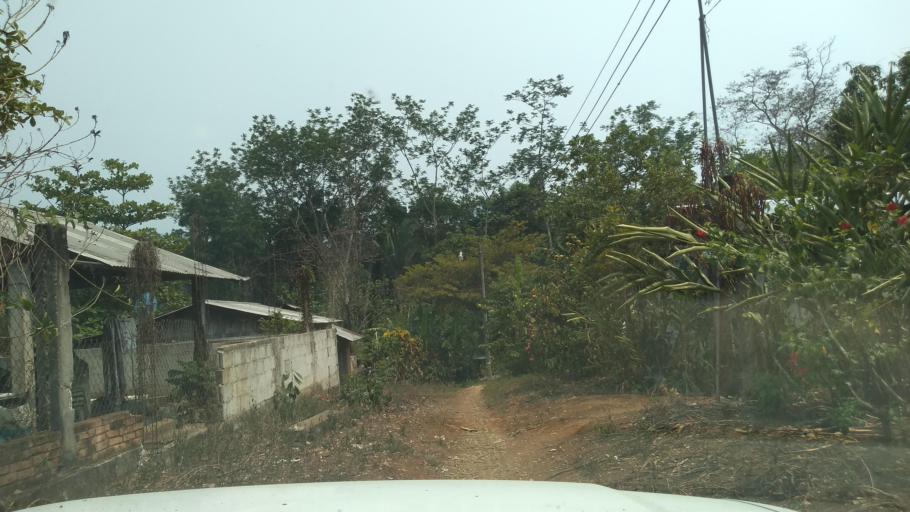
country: MX
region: Veracruz
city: Cosolapa
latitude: 18.5878
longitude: -96.7138
